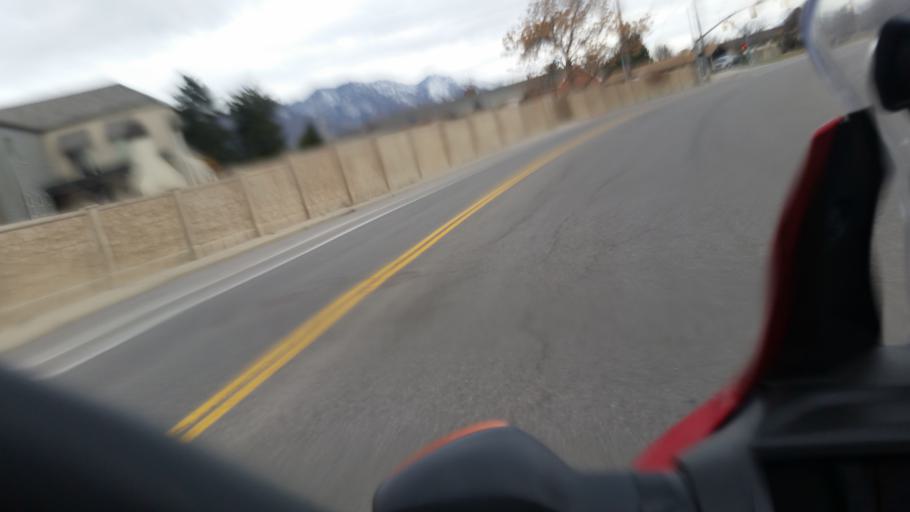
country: US
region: Utah
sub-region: Utah County
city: Orem
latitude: 40.3201
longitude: -111.6865
